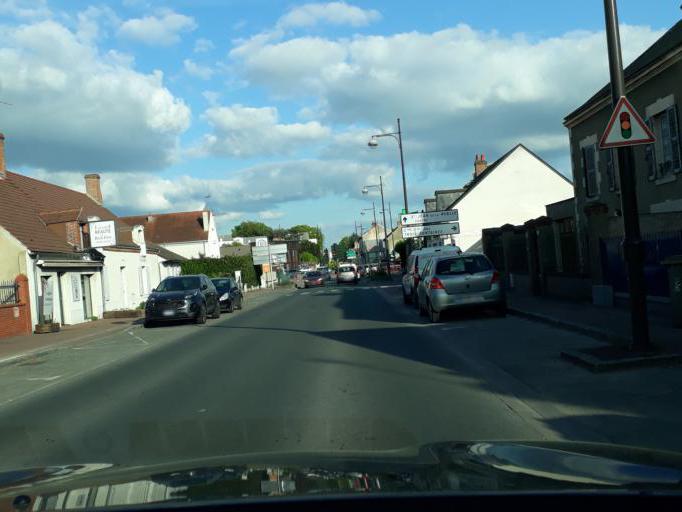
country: FR
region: Centre
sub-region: Departement du Loiret
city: Saint-Jean-de-la-Ruelle
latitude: 47.9154
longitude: 1.8672
